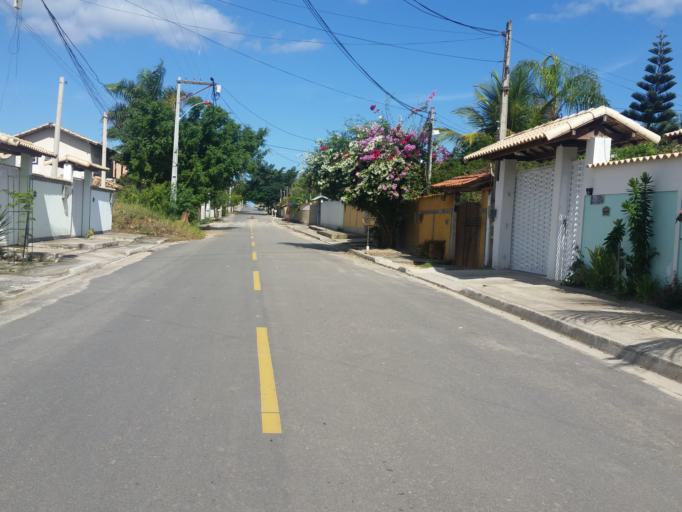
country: BR
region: Rio de Janeiro
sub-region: Marica
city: Marica
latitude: -22.9614
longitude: -42.9667
